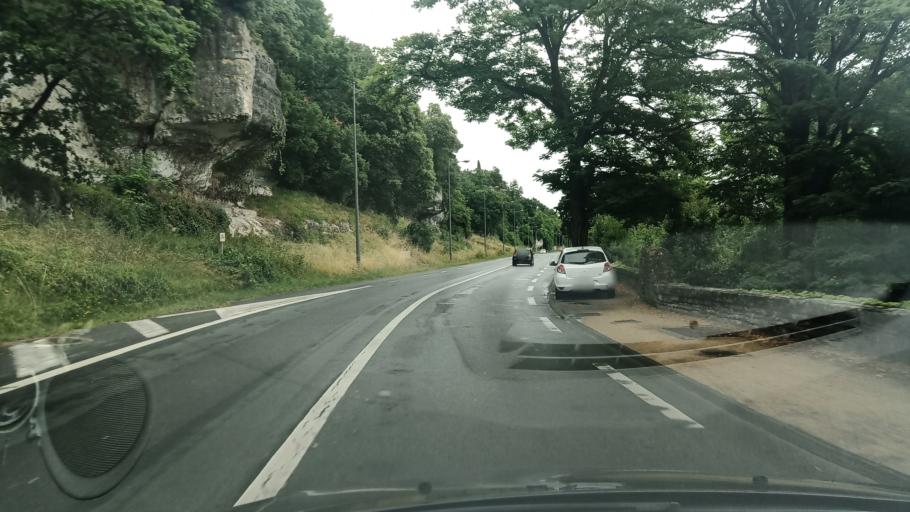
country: FR
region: Poitou-Charentes
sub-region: Departement de la Vienne
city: Poitiers
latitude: 46.5987
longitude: 0.3380
